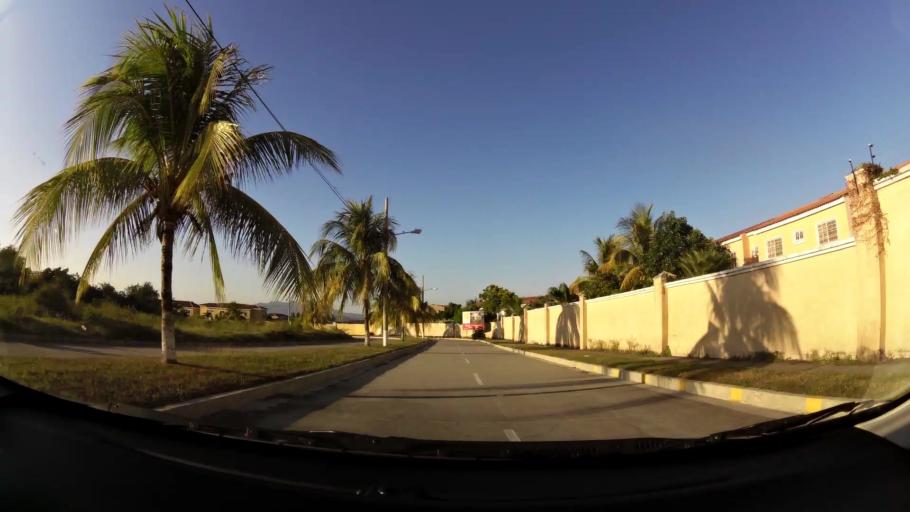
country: SV
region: La Libertad
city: Ciudad Arce
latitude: 13.7575
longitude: -89.3725
